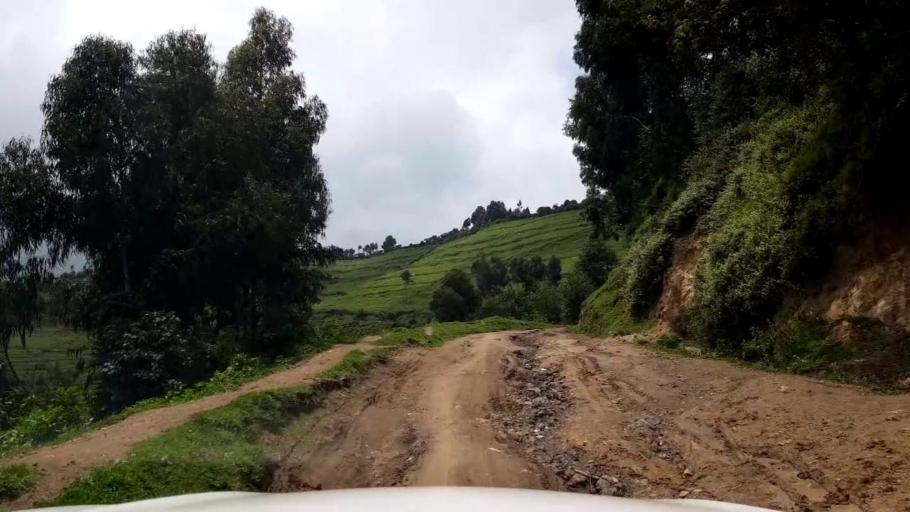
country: RW
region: Western Province
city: Gisenyi
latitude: -1.6677
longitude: 29.4120
